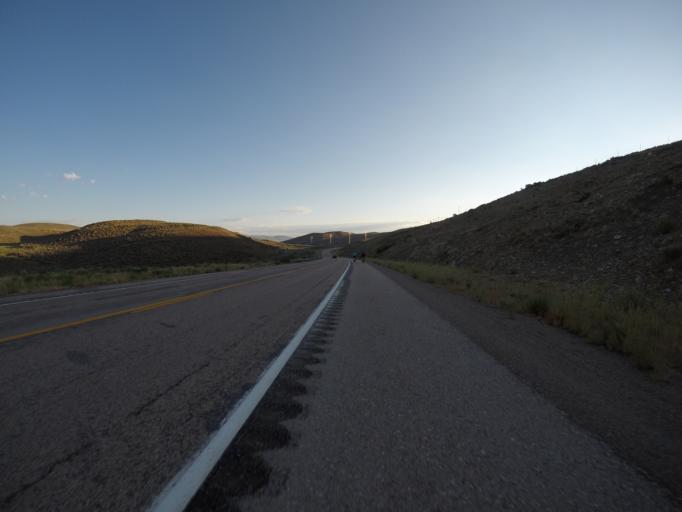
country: US
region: Wyoming
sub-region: Lincoln County
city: Kemmerer
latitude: 41.8634
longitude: -110.5273
